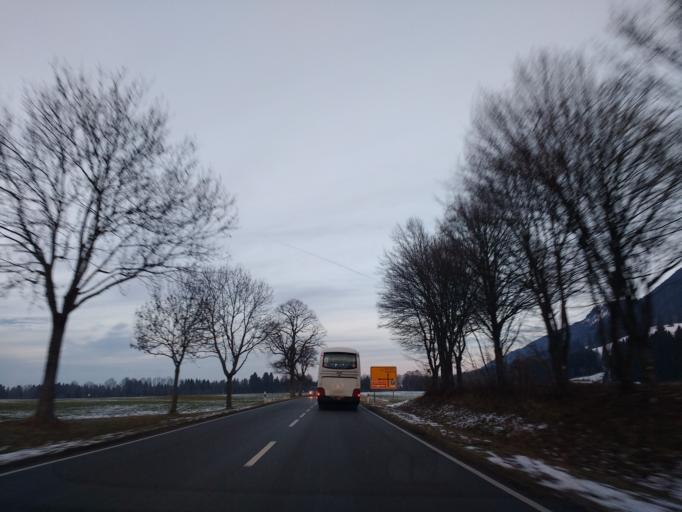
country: DE
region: Bavaria
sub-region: Swabia
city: Halblech
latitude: 47.6222
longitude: 10.8113
